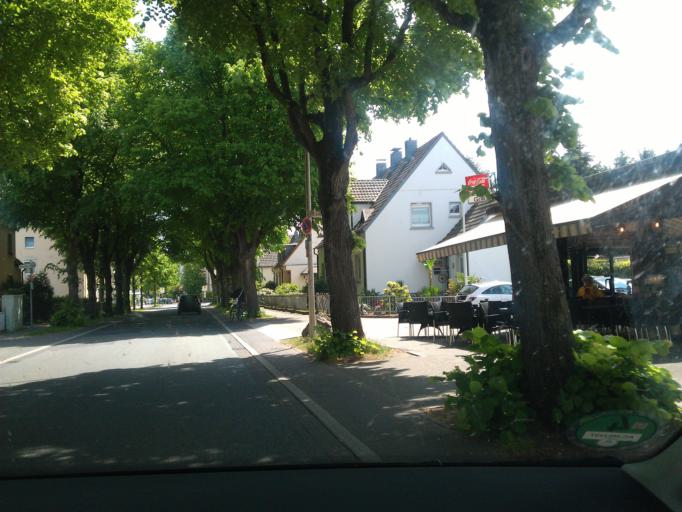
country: DE
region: North Rhine-Westphalia
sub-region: Regierungsbezirk Dusseldorf
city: Hilden
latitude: 51.1573
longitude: 6.9458
